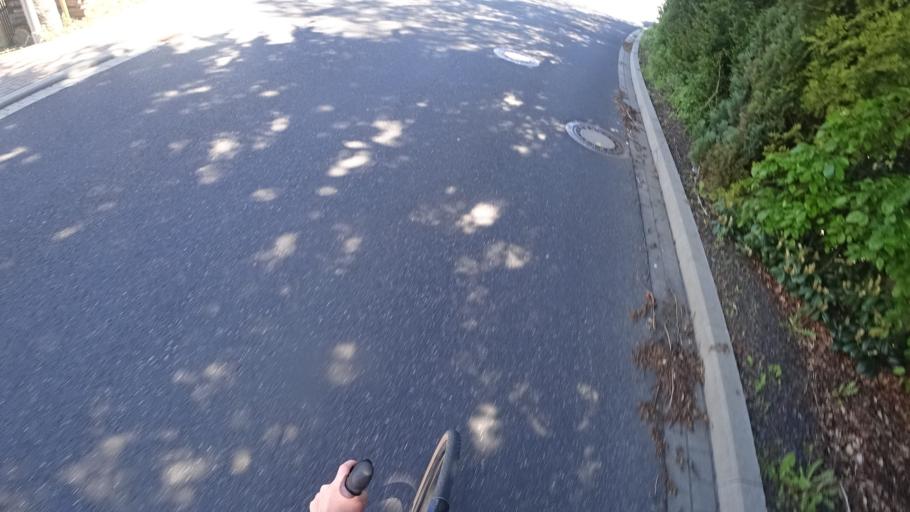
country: DE
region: Rheinland-Pfalz
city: Steineroth
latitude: 50.7423
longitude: 7.8537
